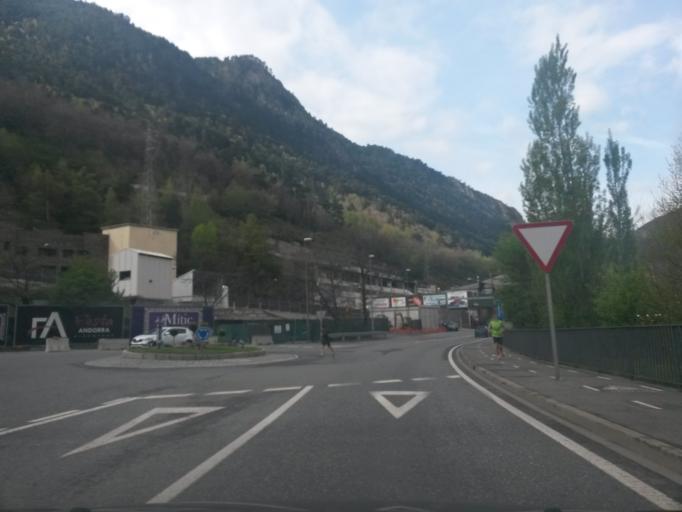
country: AD
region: Andorra la Vella
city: Andorra la Vella
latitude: 42.4985
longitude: 1.5109
